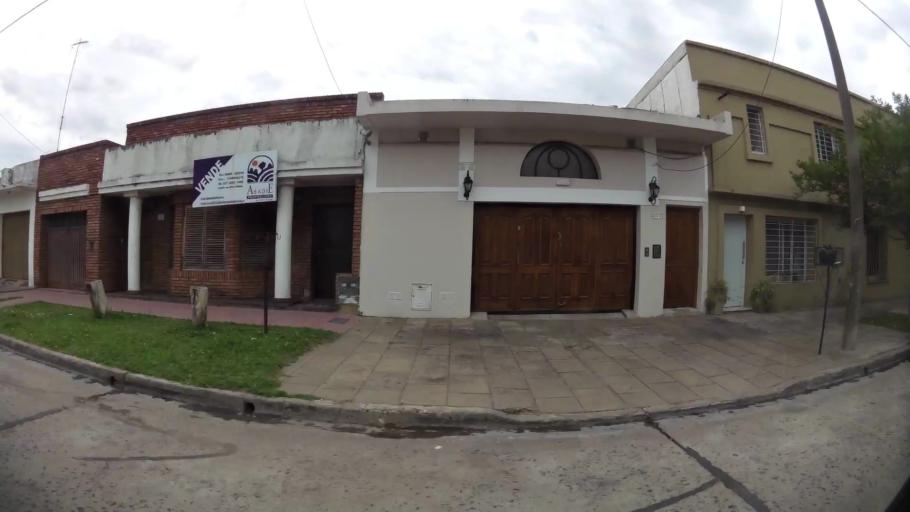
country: AR
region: Buenos Aires
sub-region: Partido de Campana
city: Campana
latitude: -34.1680
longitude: -58.9517
